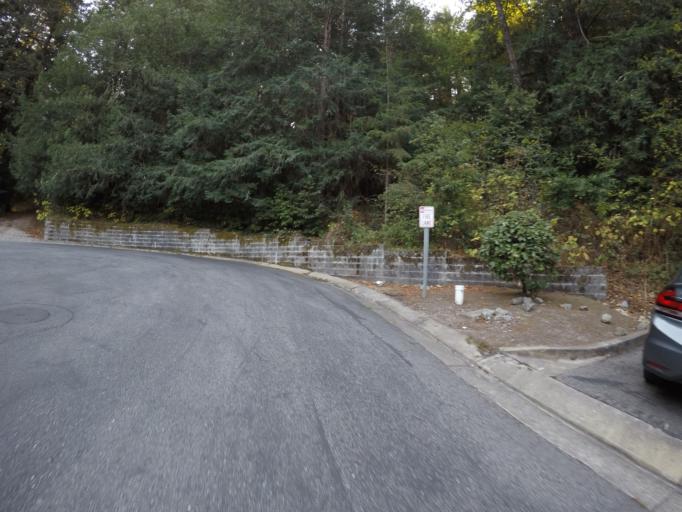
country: US
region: California
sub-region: Santa Cruz County
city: Scotts Valley
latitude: 37.0385
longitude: -122.0157
